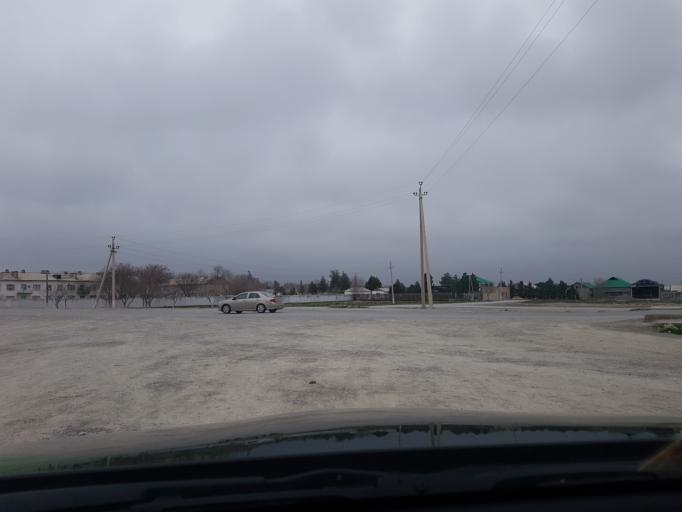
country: TM
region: Ahal
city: Abadan
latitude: 38.1406
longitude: 57.9506
